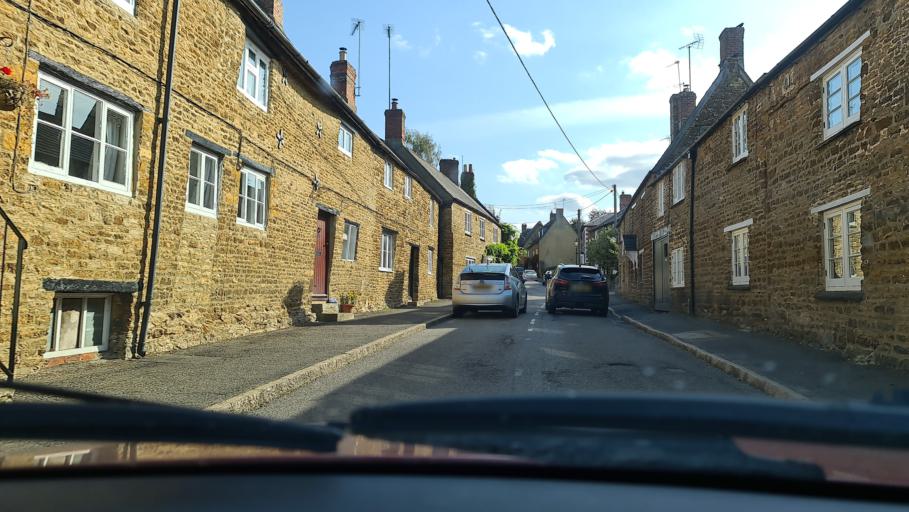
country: GB
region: England
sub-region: Oxfordshire
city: Adderbury
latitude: 52.0227
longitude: -1.2744
